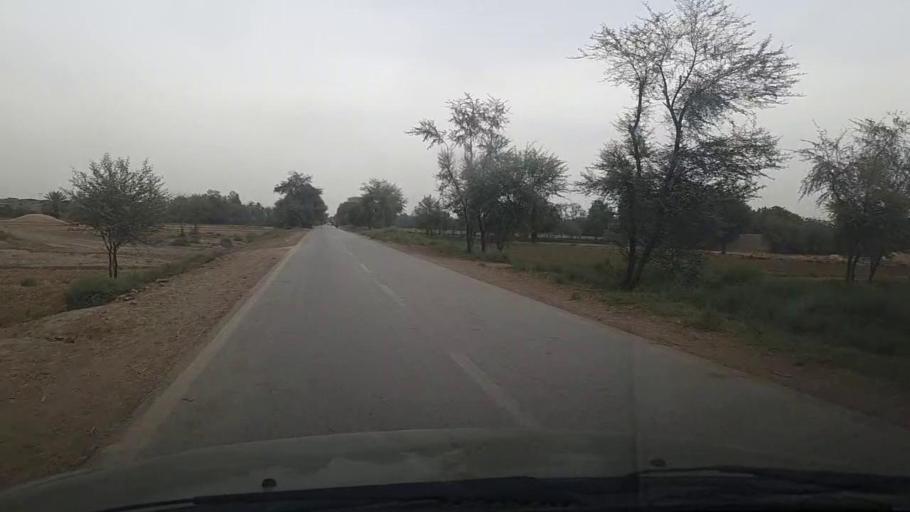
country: PK
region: Sindh
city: Daulatpur
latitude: 26.3257
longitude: 68.1094
